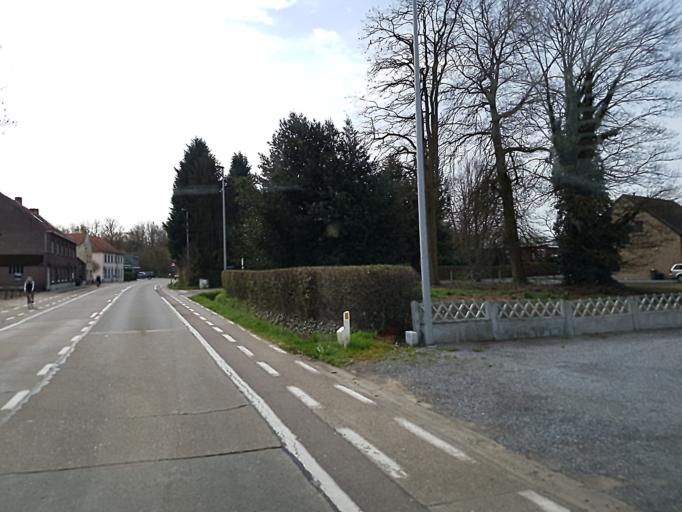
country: BE
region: Flanders
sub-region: Provincie Vlaams-Brabant
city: Scherpenheuvel-Zichem
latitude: 51.0177
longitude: 4.9910
